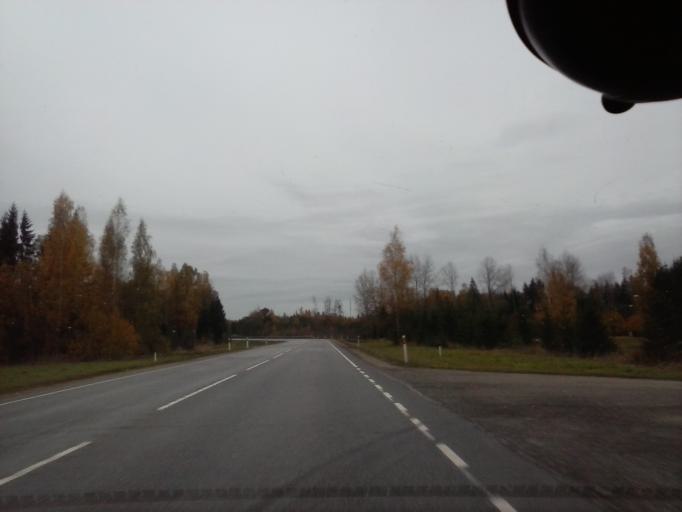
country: EE
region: Jogevamaa
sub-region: Jogeva linn
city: Jogeva
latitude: 58.5872
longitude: 26.2621
